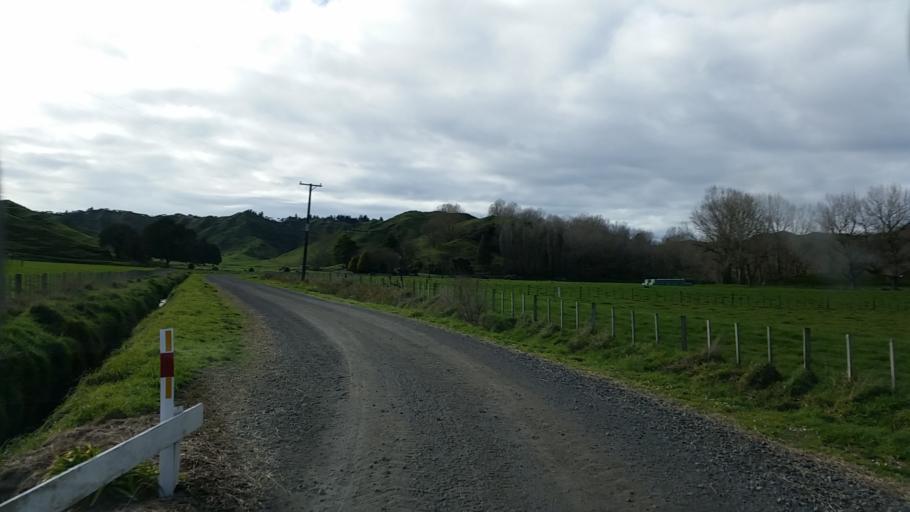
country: NZ
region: Taranaki
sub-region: South Taranaki District
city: Eltham
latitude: -39.2509
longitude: 174.5368
